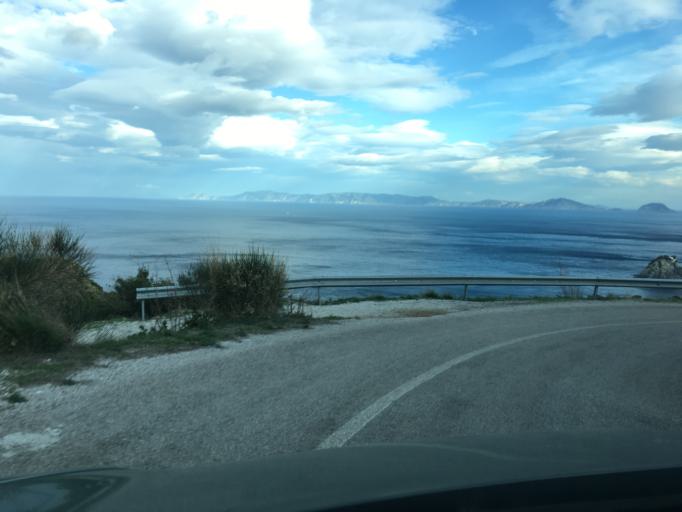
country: GR
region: Thessaly
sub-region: Nomos Magnisias
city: Skopelos
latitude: 39.1793
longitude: 23.6356
